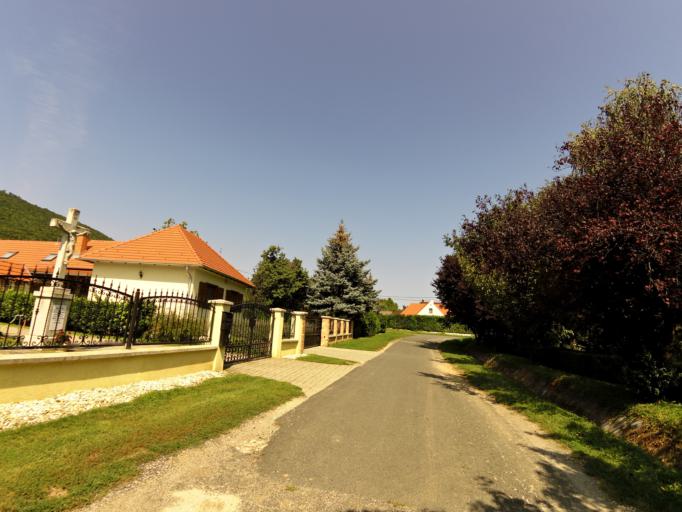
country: HU
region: Zala
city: Vonyarcvashegy
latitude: 46.8013
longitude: 17.3763
